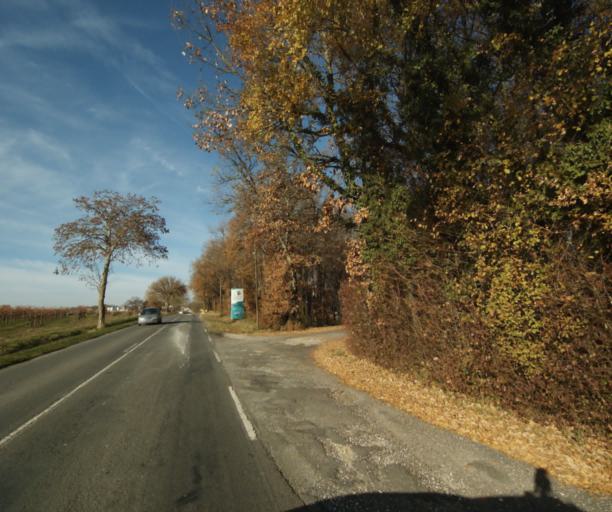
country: FR
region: Poitou-Charentes
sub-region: Departement de la Charente-Maritime
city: Burie
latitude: 45.7693
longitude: -0.4116
